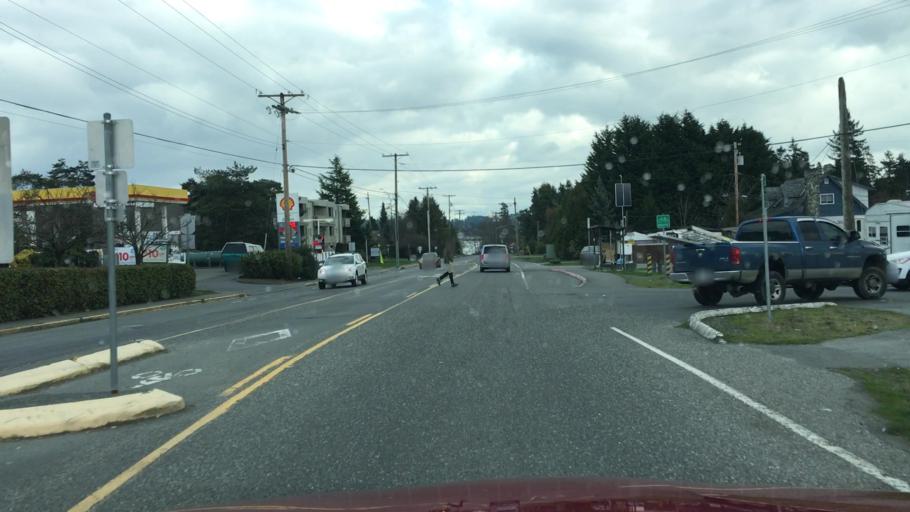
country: CA
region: British Columbia
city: North Saanich
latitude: 48.5942
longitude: -123.3970
